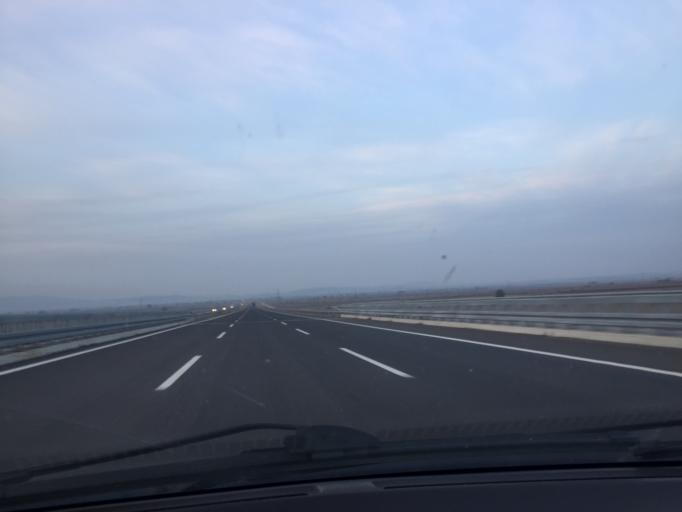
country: TR
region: Manisa
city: Halitpasa
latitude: 38.7062
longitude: 27.6455
